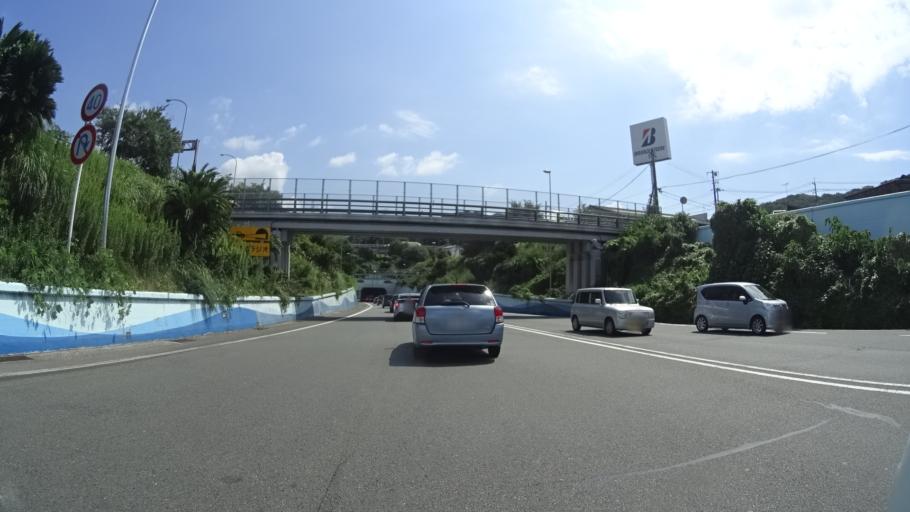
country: JP
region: Yamaguchi
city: Shimonoseki
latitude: 33.9763
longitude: 130.9469
